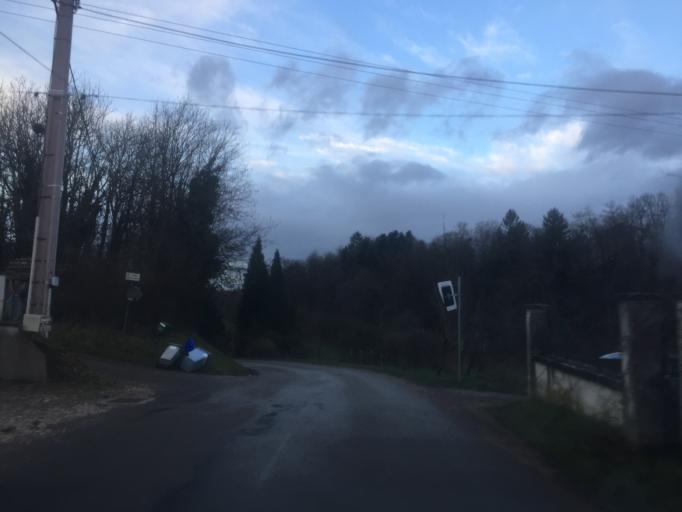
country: FR
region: Franche-Comte
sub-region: Departement du Jura
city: Orchamps
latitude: 47.1306
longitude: 5.6604
